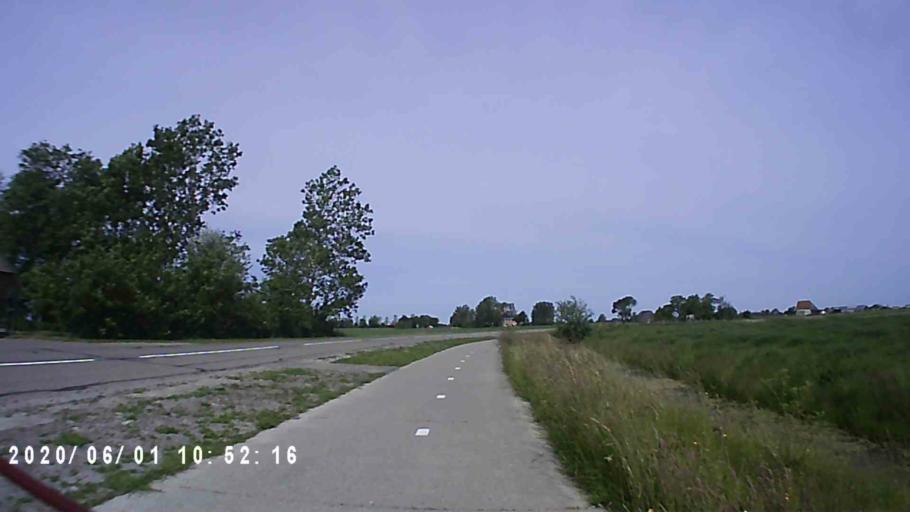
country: NL
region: Friesland
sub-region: Gemeente Franekeradeel
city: Franeker
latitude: 53.1994
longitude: 5.5189
